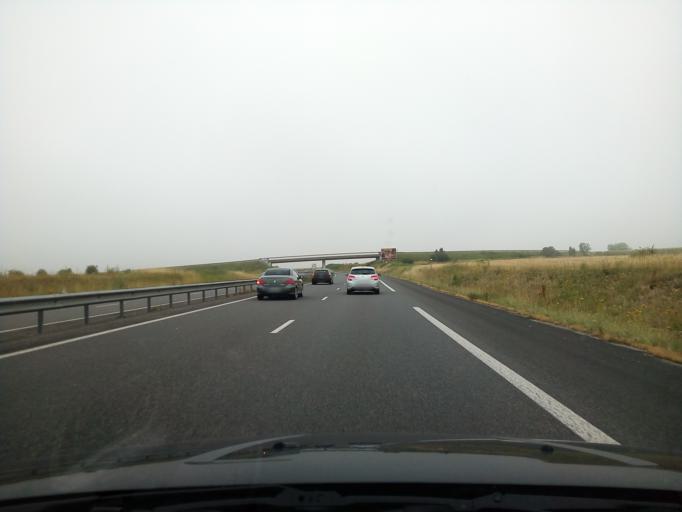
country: FR
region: Poitou-Charentes
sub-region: Departement de la Charente
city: Jarnac
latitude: 45.6977
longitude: -0.1211
